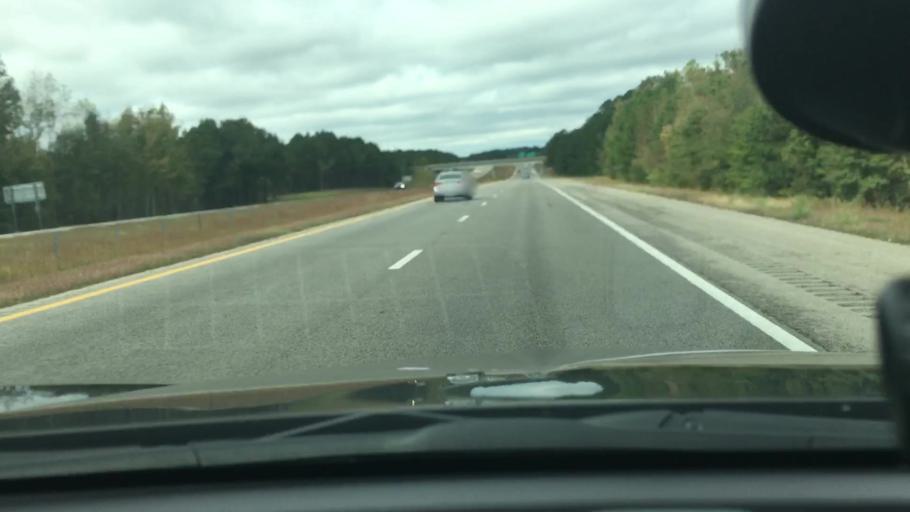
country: US
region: North Carolina
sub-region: Wilson County
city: Lucama
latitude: 35.7237
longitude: -78.0068
